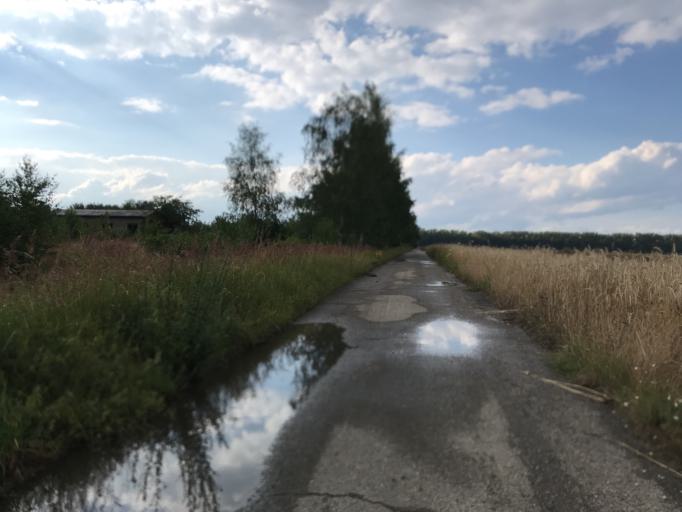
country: CZ
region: Jihocesky
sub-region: Okres Jindrichuv Hradec
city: Trebon
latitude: 49.0195
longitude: 14.7599
